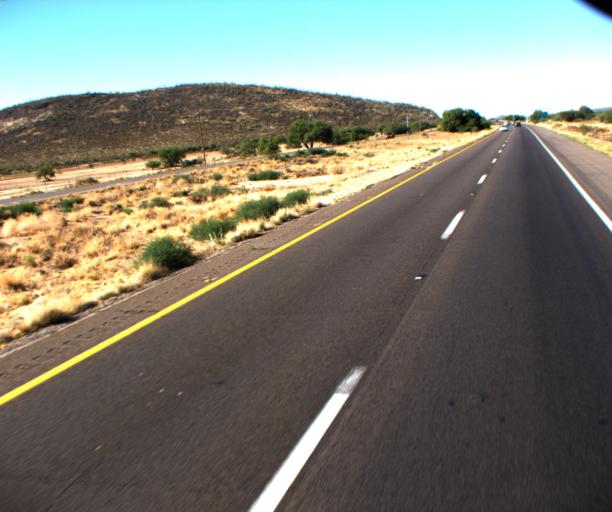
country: US
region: Arizona
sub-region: Pima County
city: Drexel Heights
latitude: 32.1152
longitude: -110.9907
